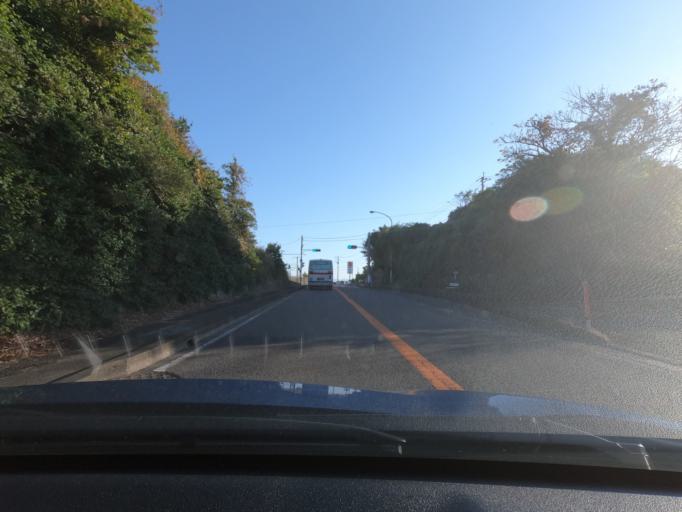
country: JP
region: Kagoshima
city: Akune
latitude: 31.9781
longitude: 130.2040
